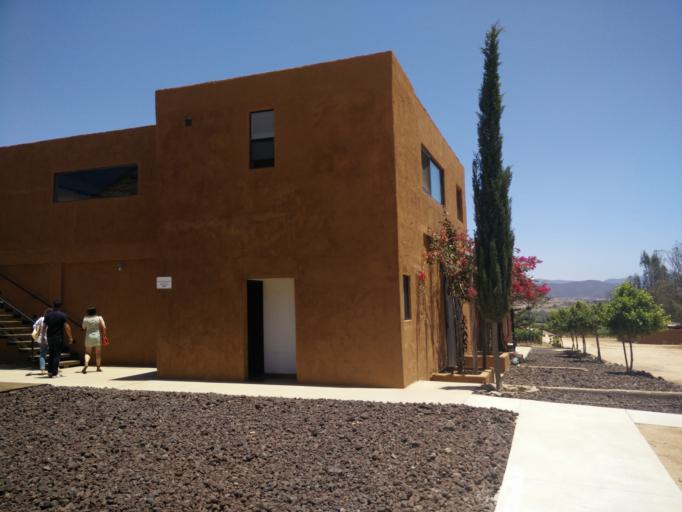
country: MX
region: Baja California
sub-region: Ensenada
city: Rancho Verde
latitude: 32.0512
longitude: -116.6689
